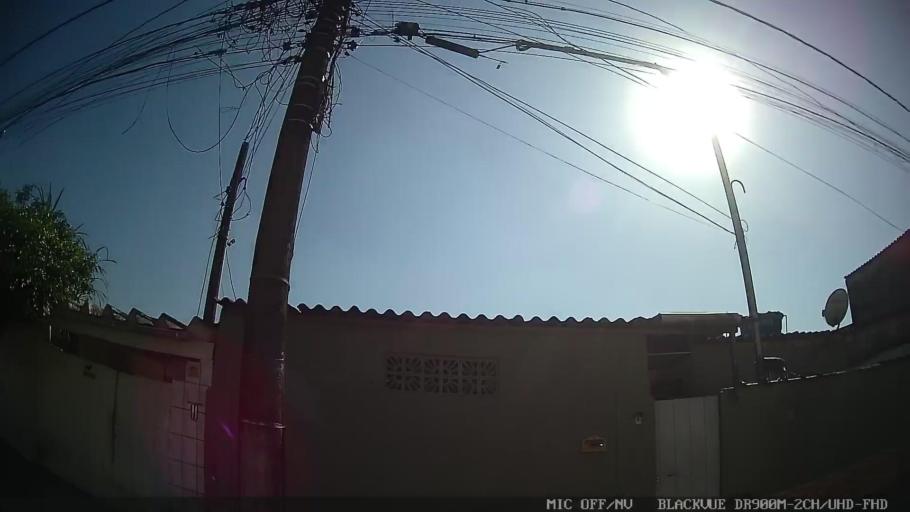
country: BR
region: Sao Paulo
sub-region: Santos
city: Santos
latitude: -23.9449
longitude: -46.2951
